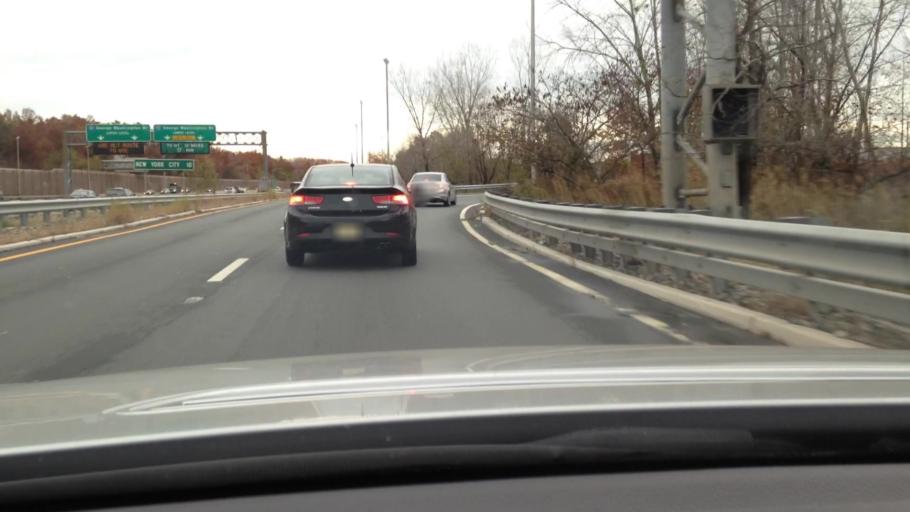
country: US
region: New Jersey
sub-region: Bergen County
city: Saddle Brook
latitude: 40.9030
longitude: -74.0963
